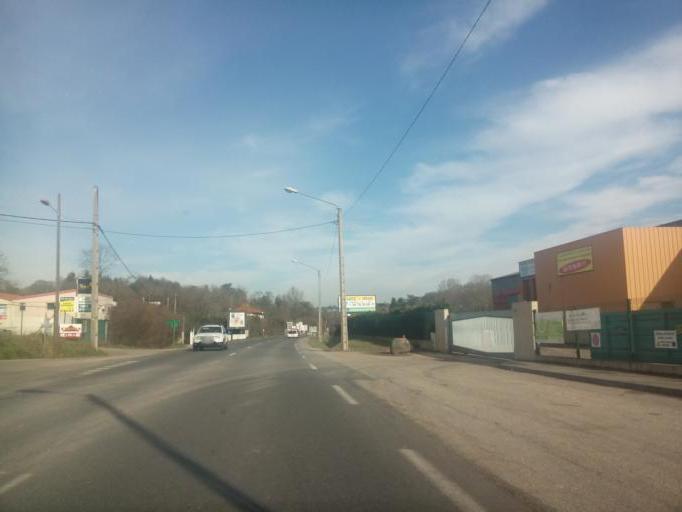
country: FR
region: Rhone-Alpes
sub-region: Departement du Rhone
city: Saint-Genis-Laval
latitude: 45.7116
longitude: 4.7720
